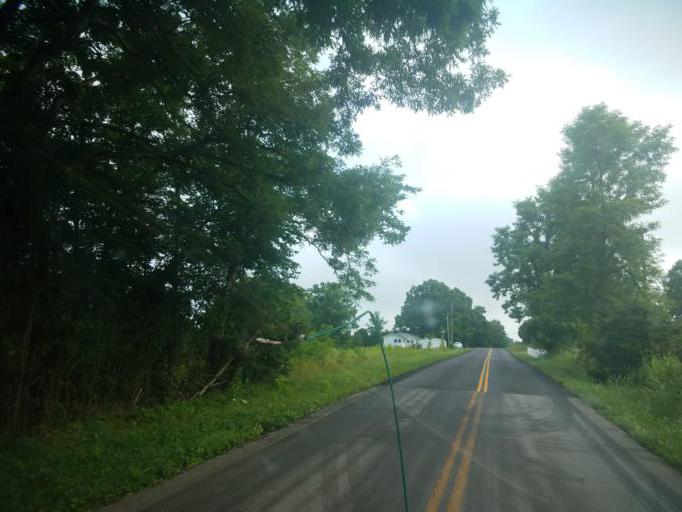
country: US
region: Kentucky
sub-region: Clinton County
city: Albany
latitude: 36.7773
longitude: -85.1415
